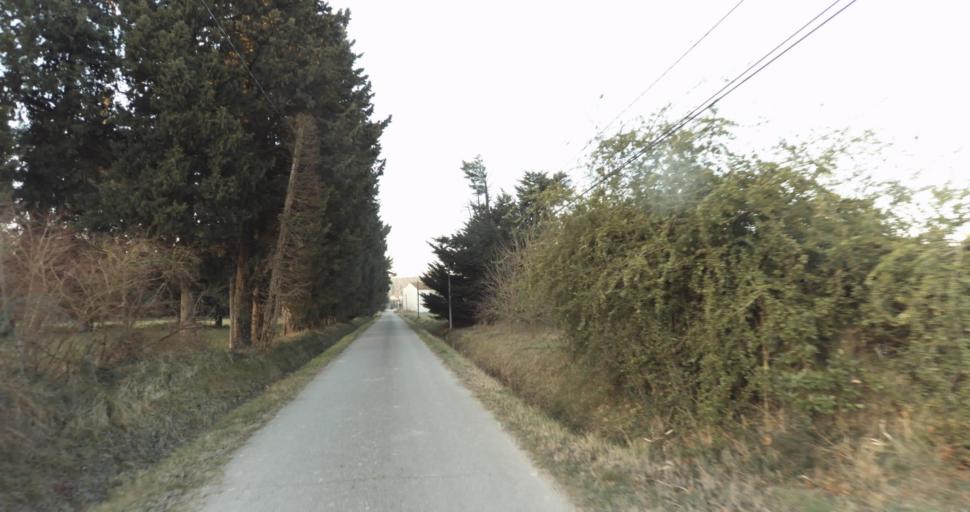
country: FR
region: Provence-Alpes-Cote d'Azur
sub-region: Departement des Bouches-du-Rhone
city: Barbentane
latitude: 43.9039
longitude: 4.7721
